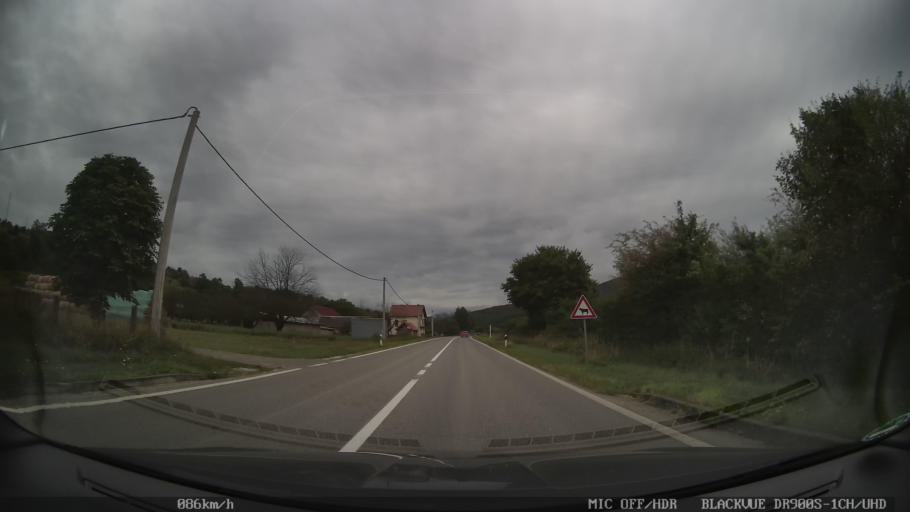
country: HR
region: Licko-Senjska
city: Otocac
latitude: 44.8574
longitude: 15.3239
